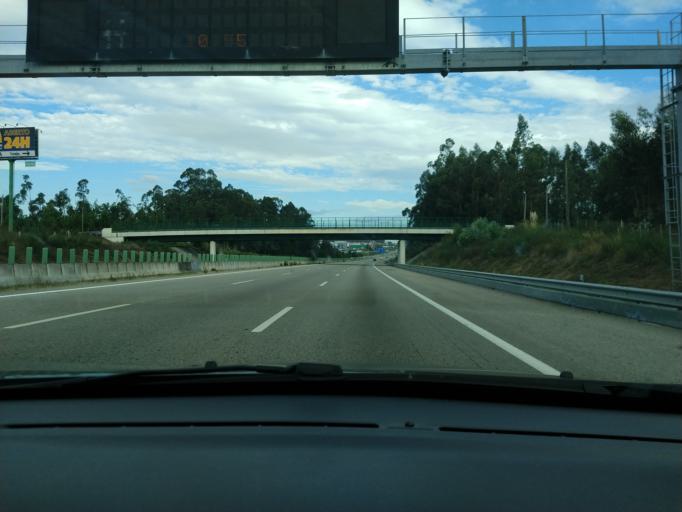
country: PT
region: Aveiro
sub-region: Santa Maria da Feira
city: Feira
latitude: 40.9103
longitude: -8.5674
